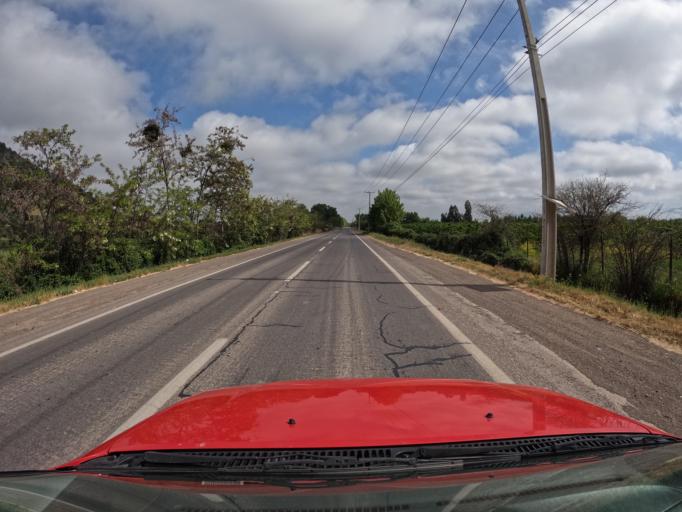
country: CL
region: O'Higgins
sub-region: Provincia de Colchagua
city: Santa Cruz
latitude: -34.7038
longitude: -71.3043
